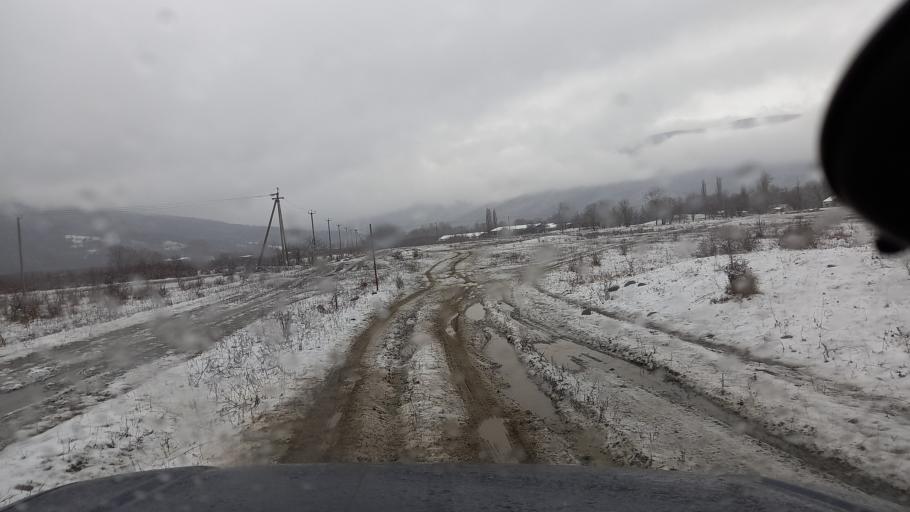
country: RU
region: Adygeya
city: Kamennomostskiy
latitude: 44.2203
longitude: 40.1795
